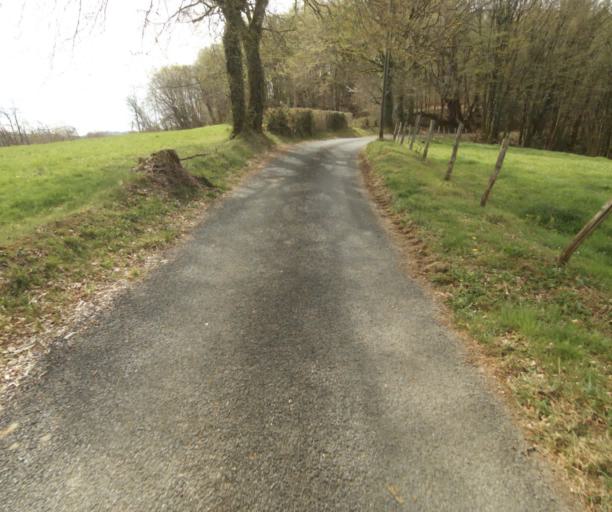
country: FR
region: Limousin
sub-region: Departement de la Correze
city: Naves
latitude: 45.3303
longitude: 1.8027
